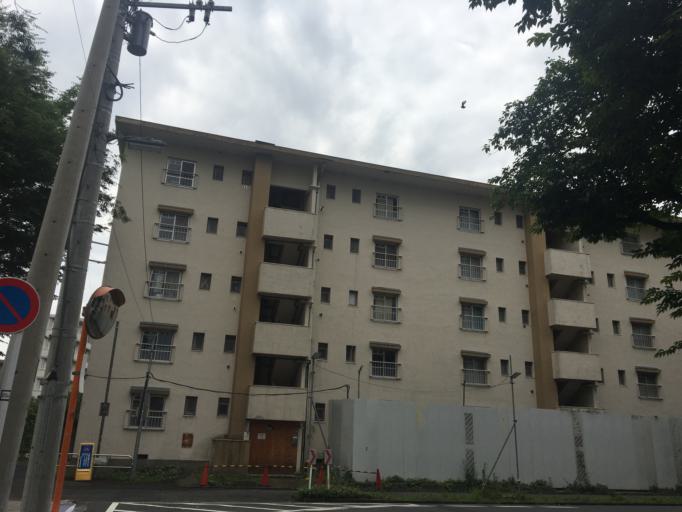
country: JP
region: Saitama
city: Kawaguchi
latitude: 35.7775
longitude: 139.7159
